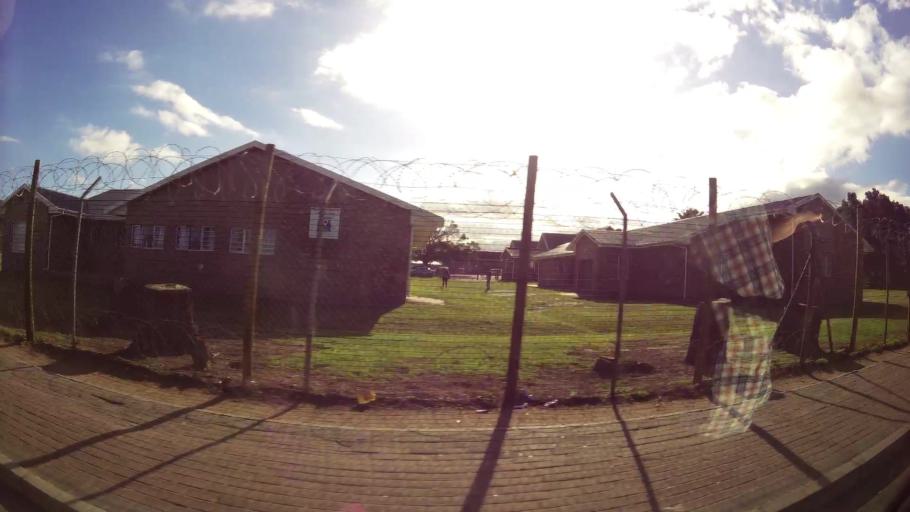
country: ZA
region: Western Cape
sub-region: Eden District Municipality
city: George
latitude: -33.9747
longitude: 22.4798
